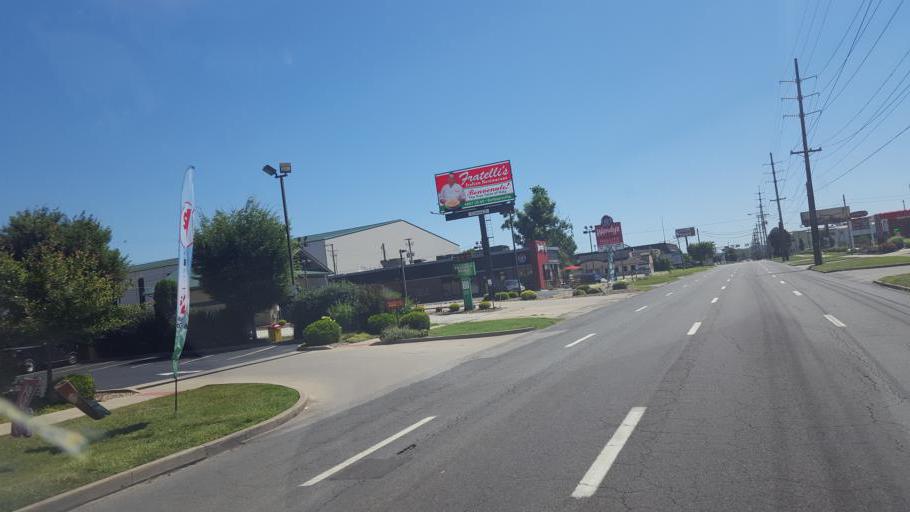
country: US
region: West Virginia
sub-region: Cabell County
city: Huntington
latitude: 38.4234
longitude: -82.4204
